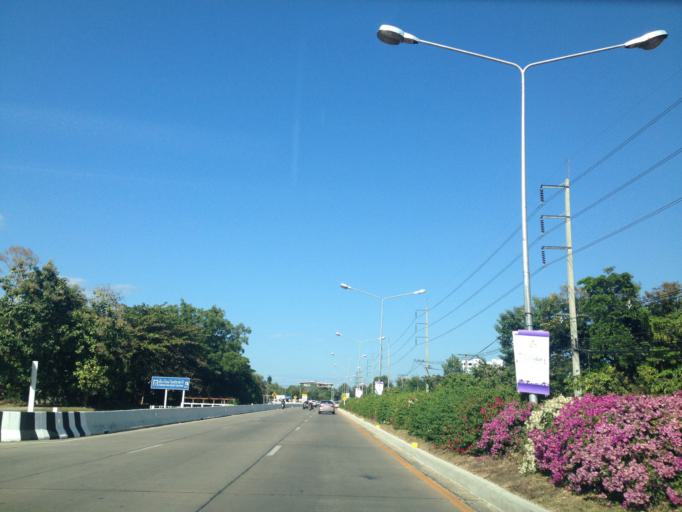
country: TH
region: Chiang Mai
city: Chiang Mai
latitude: 18.8139
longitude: 98.9634
